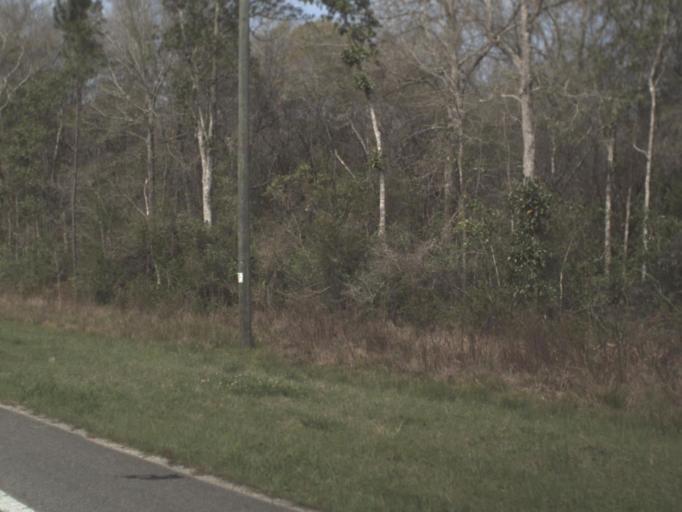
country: US
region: Florida
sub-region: Gadsden County
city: Quincy
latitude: 30.3883
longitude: -84.6991
